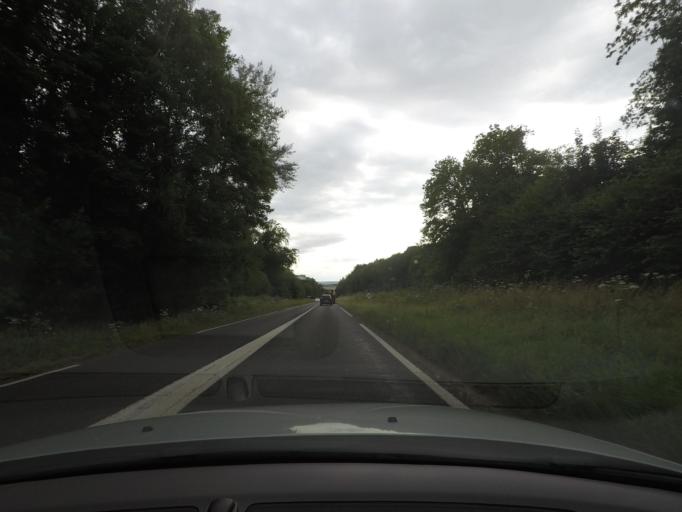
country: FR
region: Haute-Normandie
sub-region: Departement de la Seine-Maritime
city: Ymare
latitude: 49.3543
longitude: 1.1717
